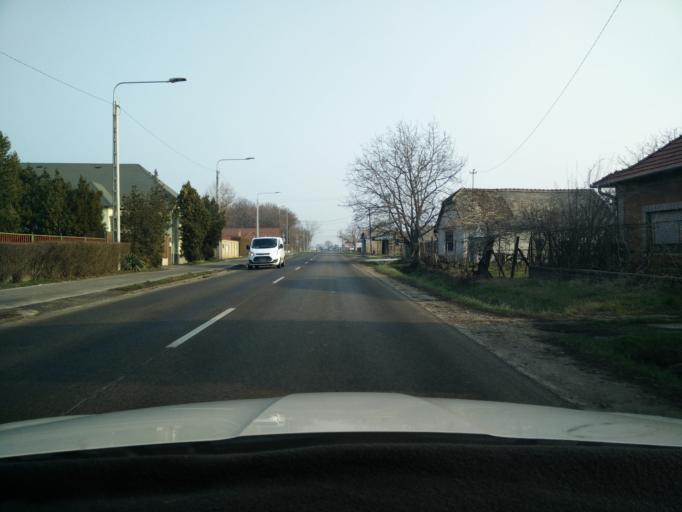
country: HU
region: Tolna
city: Szekszard
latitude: 46.3176
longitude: 18.6966
